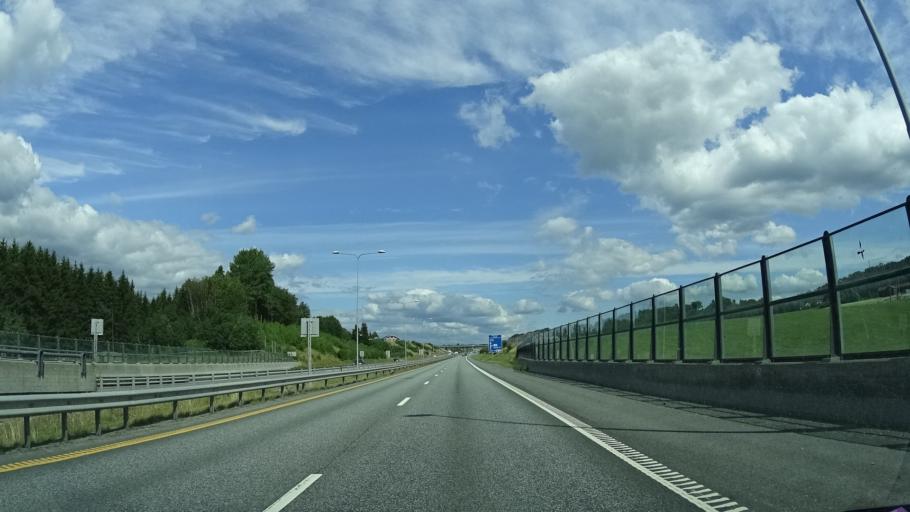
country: NO
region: Vestfold
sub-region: Sande
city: Sande
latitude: 59.6468
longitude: 10.2217
